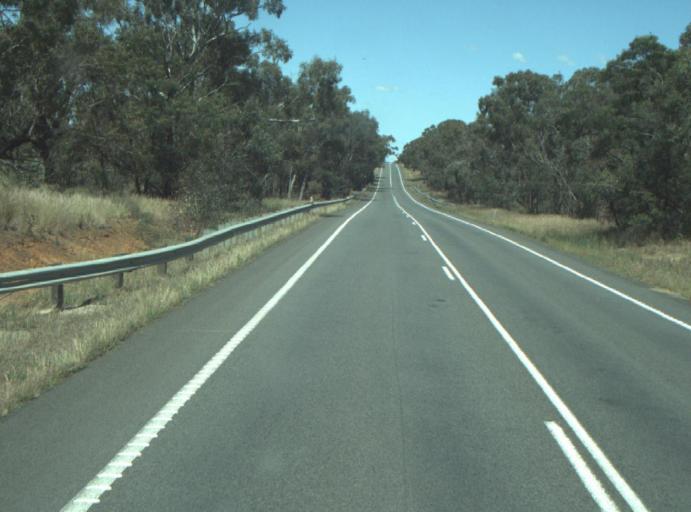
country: AU
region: Victoria
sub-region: Greater Geelong
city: Lara
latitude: -37.9146
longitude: 144.3670
